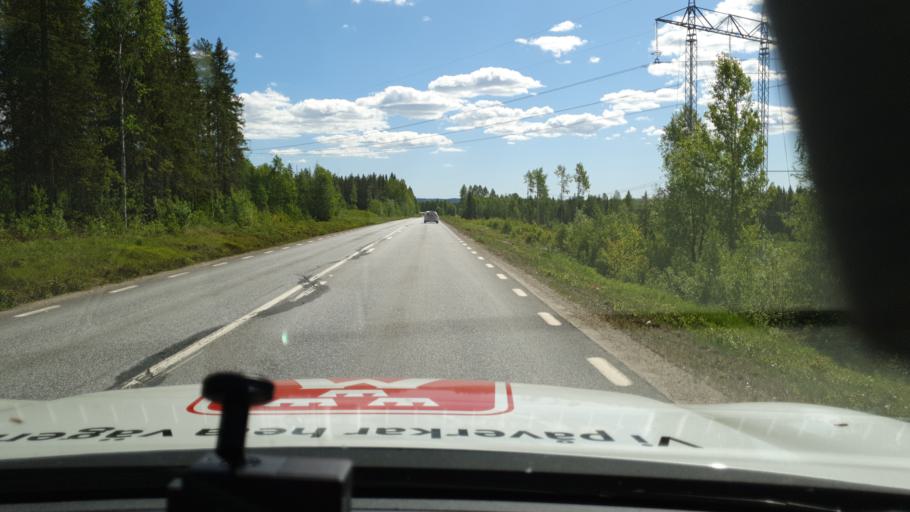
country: SE
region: Vaesterbotten
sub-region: Vannas Kommun
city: Vaennaes
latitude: 63.9766
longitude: 19.7322
